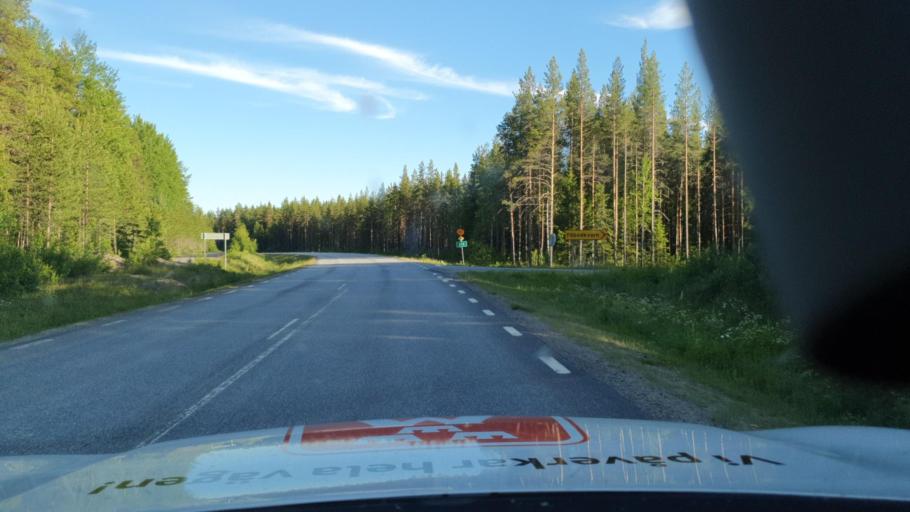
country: SE
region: Vaesterbotten
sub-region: Vannas Kommun
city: Vaennaes
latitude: 63.9495
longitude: 19.7583
